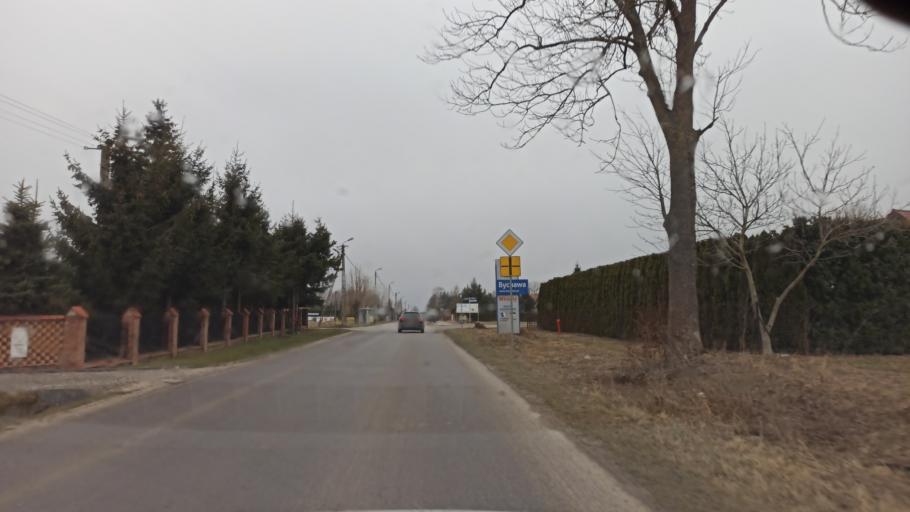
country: PL
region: Lublin Voivodeship
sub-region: Powiat lubelski
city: Bychawa
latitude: 51.0041
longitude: 22.5576
